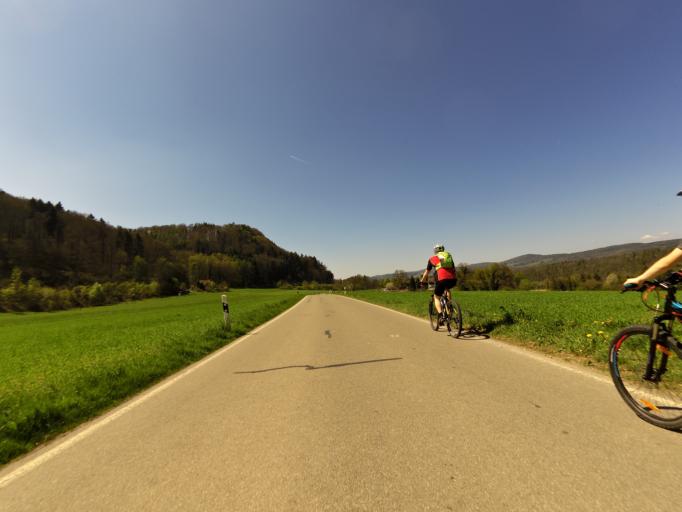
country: CH
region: Zurich
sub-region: Bezirk Buelach
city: Seglingen
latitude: 47.5763
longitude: 8.5074
